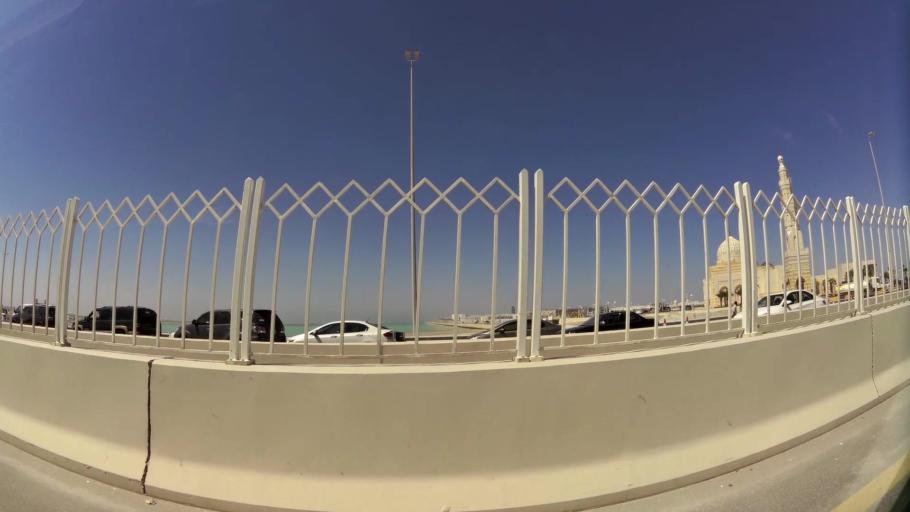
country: BH
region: Muharraq
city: Al Muharraq
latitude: 26.2943
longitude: 50.6419
